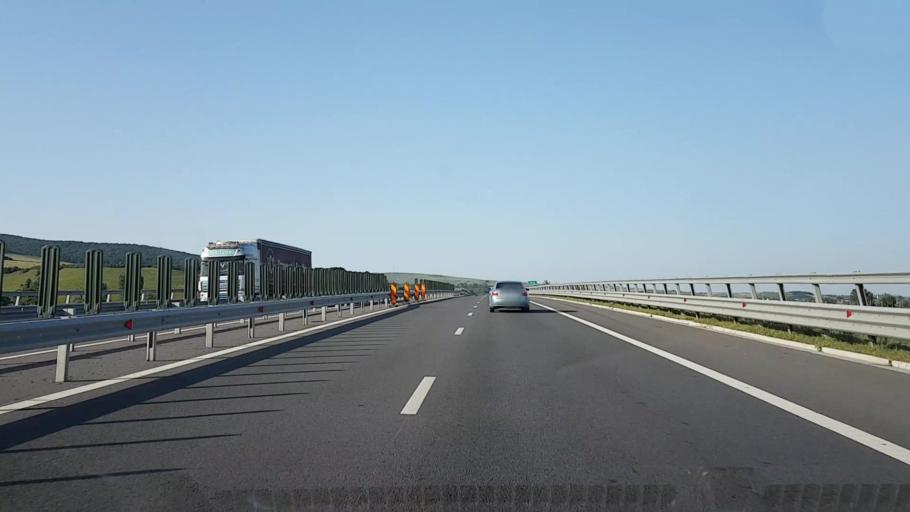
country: RO
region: Alba
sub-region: Comuna Miraslau
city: Miraslau
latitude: 46.3706
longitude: 23.7415
